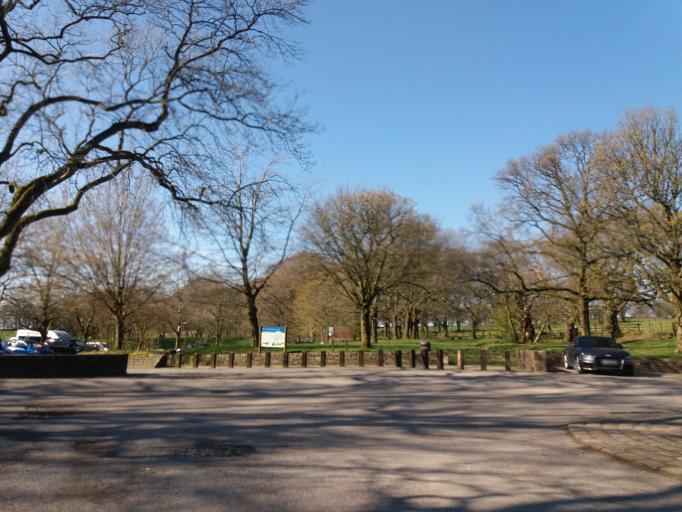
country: GB
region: England
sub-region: Borough of Bolton
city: Horwich
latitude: 53.6258
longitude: -2.5565
